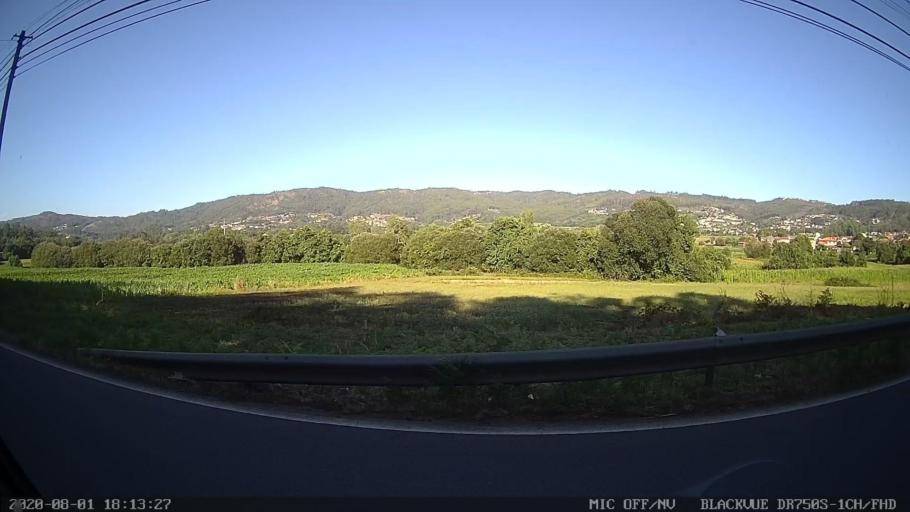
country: PT
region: Porto
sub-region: Pacos de Ferreira
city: Seroa
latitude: 41.2809
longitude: -8.4698
